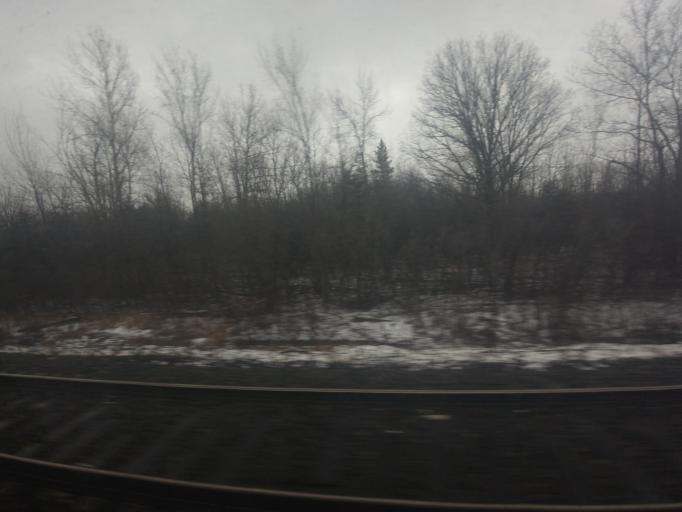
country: CA
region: Ontario
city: Deseronto
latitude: 44.2121
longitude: -77.1919
